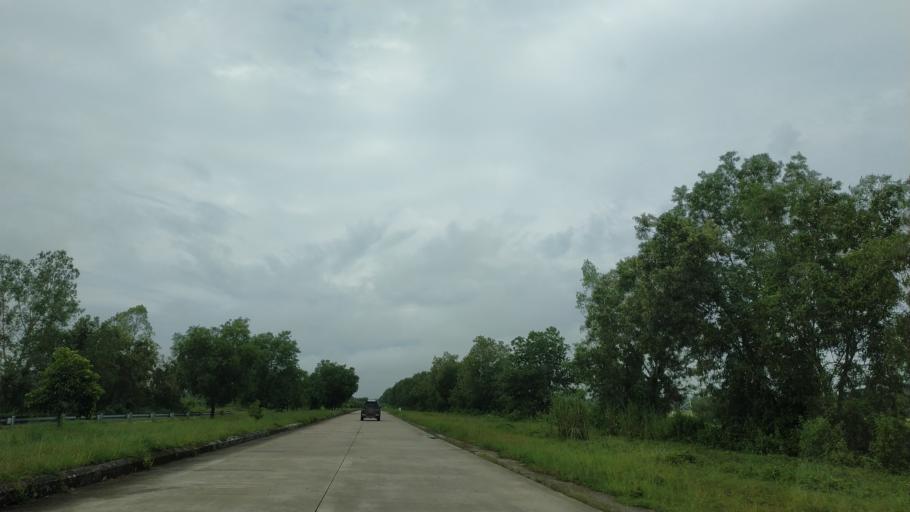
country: MM
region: Bago
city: Bago
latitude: 17.4248
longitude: 96.3677
